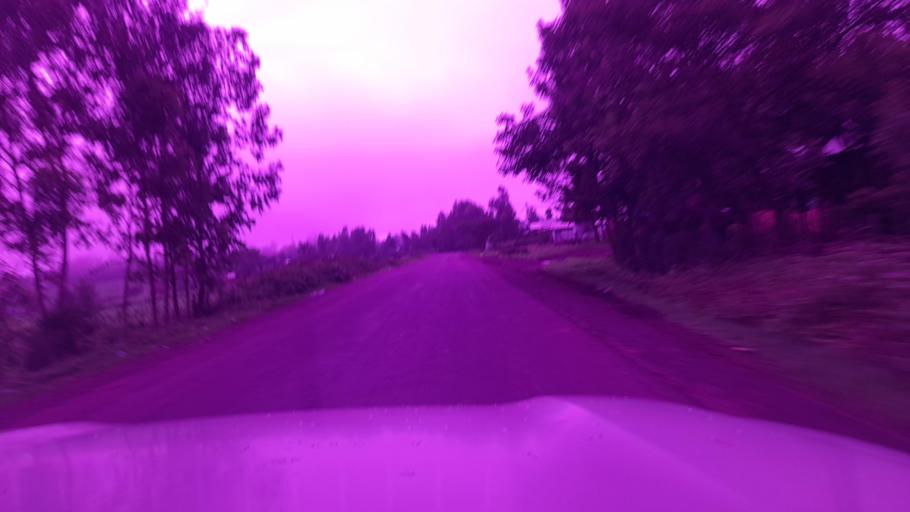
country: ET
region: Oromiya
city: Waliso
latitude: 8.1748
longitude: 37.5647
